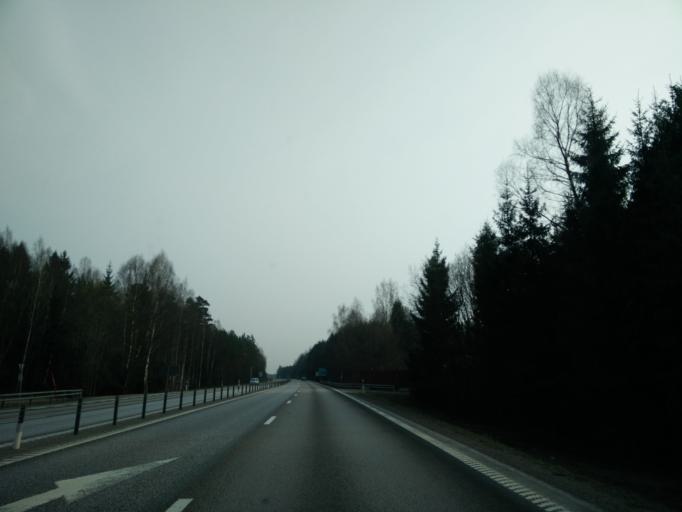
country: SE
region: Vaermland
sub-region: Karlstads Kommun
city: Karlstad
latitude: 59.4006
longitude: 13.4167
